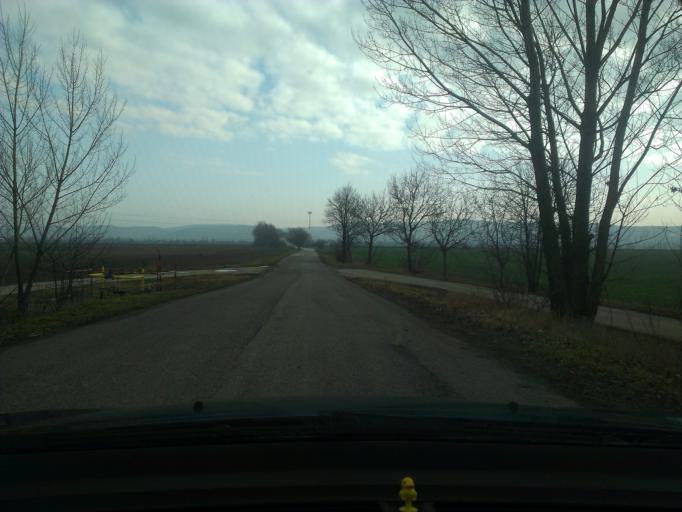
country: SK
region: Trnavsky
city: Leopoldov
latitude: 48.5205
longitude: 17.7796
